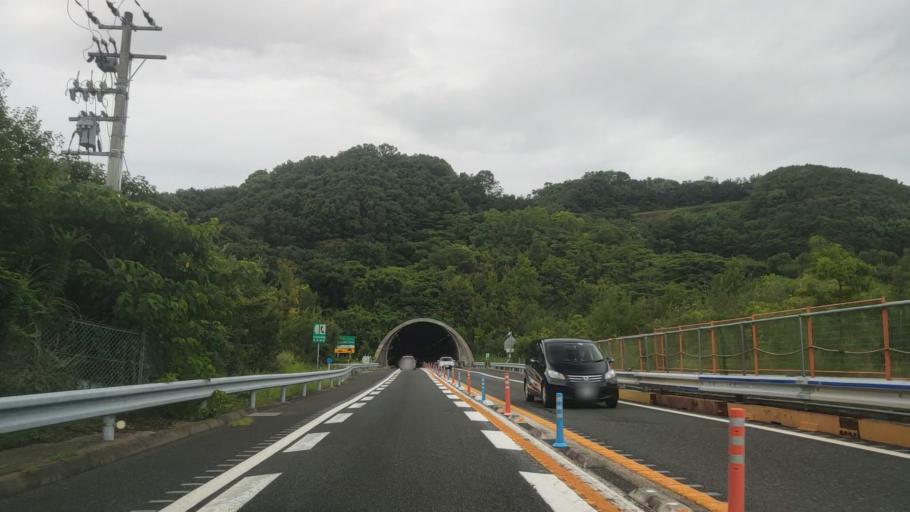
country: JP
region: Wakayama
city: Tanabe
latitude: 33.7849
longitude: 135.3124
